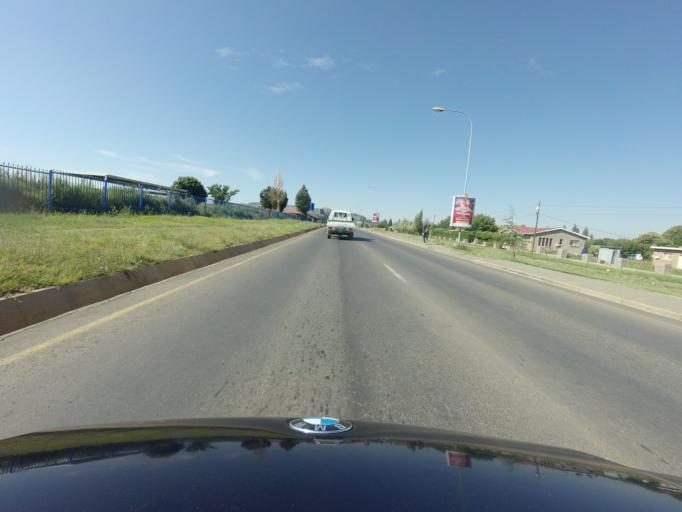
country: LS
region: Maseru
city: Maseru
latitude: -29.3025
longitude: 27.5013
